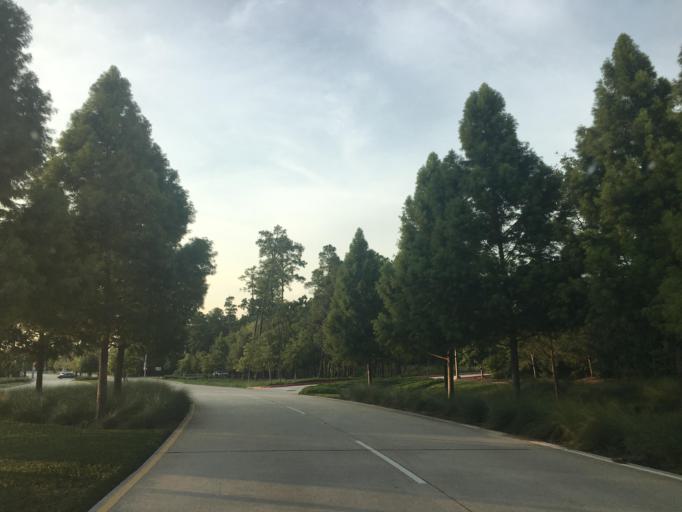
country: US
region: Texas
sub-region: Harris County
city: Spring
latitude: 30.1026
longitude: -95.4384
